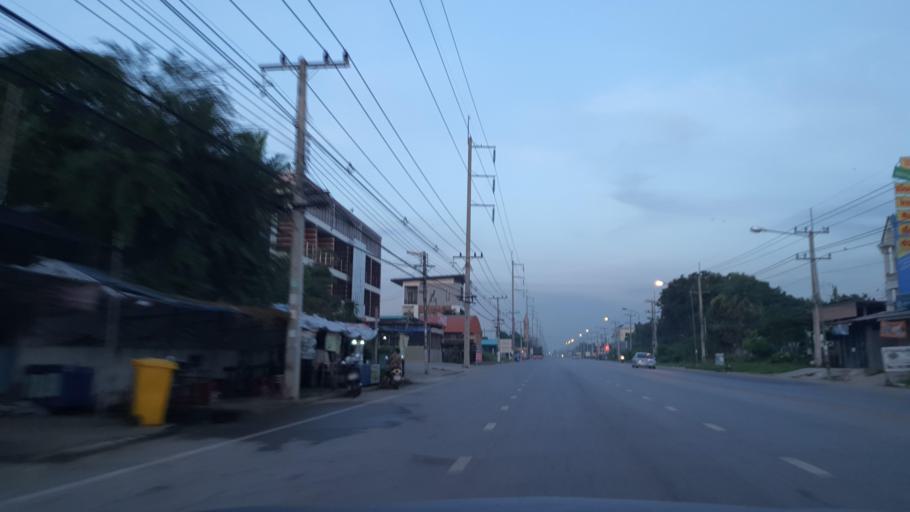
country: TH
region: Nakhon Sawan
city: Kao Liao
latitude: 15.7670
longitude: 99.9838
